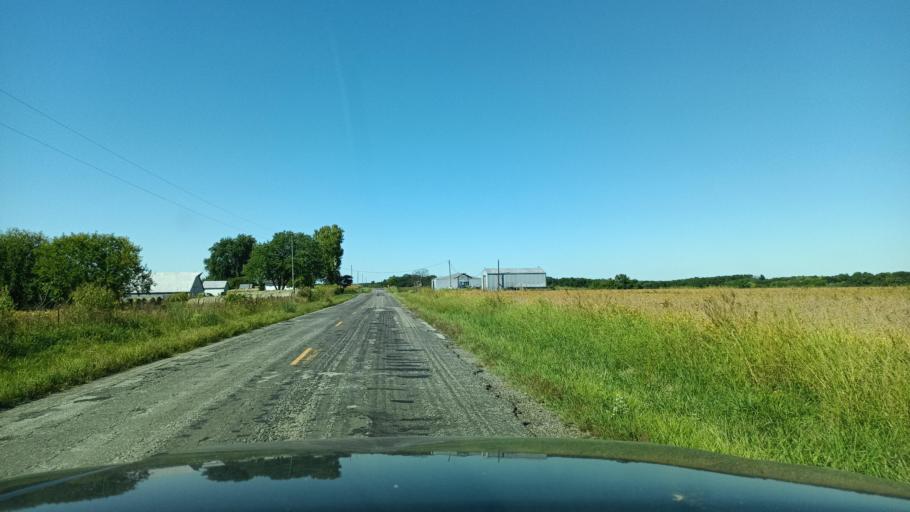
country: US
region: Missouri
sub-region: Scotland County
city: Memphis
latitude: 40.3548
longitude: -92.2274
